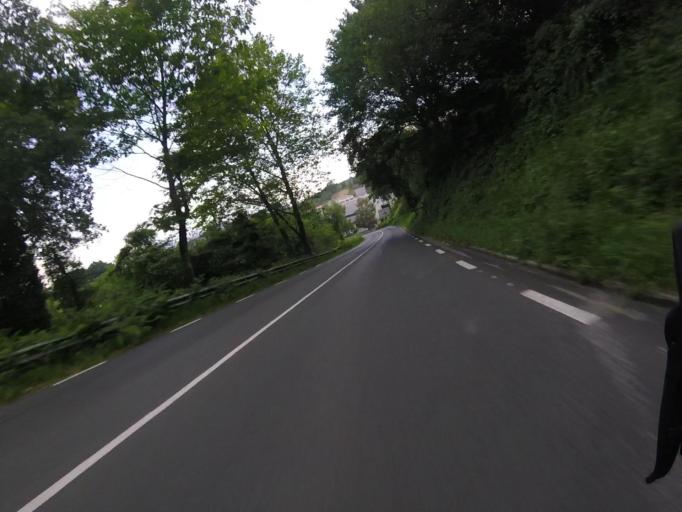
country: ES
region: Basque Country
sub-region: Provincia de Guipuzcoa
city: Errenteria
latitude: 43.3010
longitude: -1.9062
